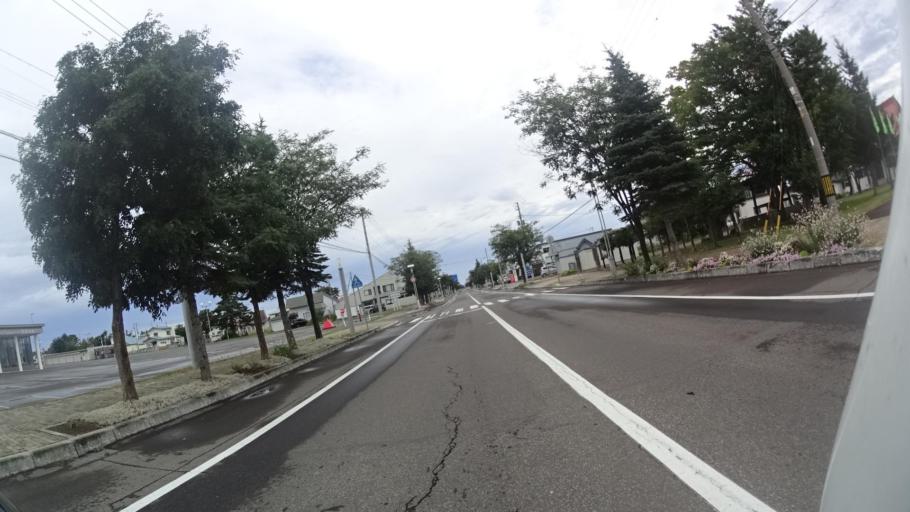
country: JP
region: Hokkaido
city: Abashiri
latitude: 43.8351
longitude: 144.5962
